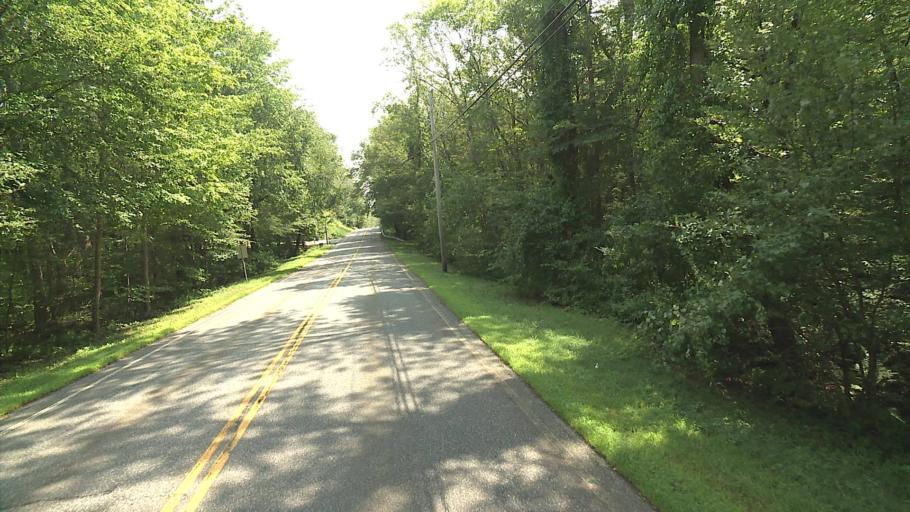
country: US
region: Connecticut
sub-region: New London County
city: Montville Center
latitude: 41.5024
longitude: -72.1839
